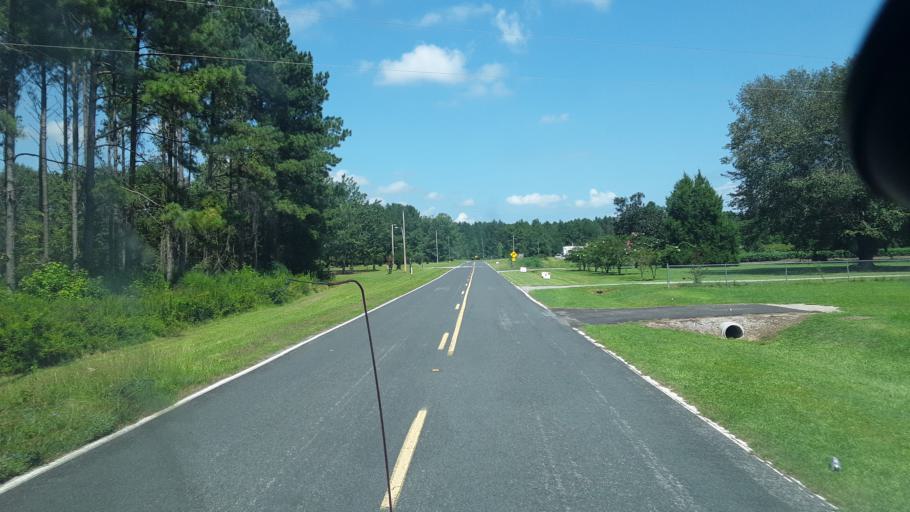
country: US
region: South Carolina
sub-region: Bamberg County
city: Bamberg
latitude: 33.3649
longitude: -81.0167
